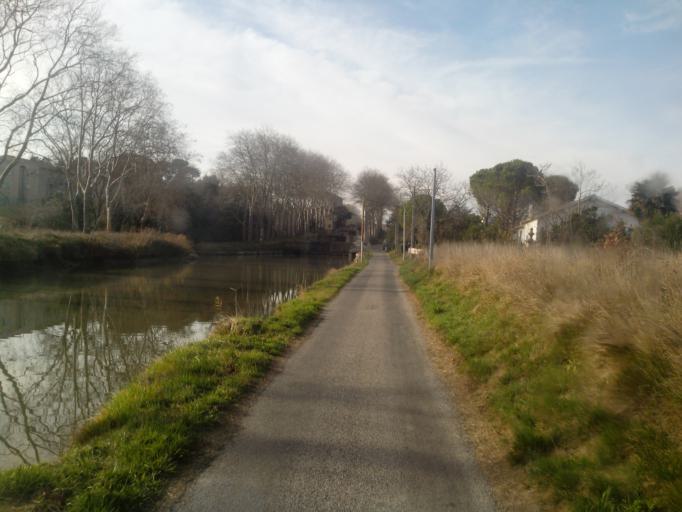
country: FR
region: Languedoc-Roussillon
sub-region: Departement de l'Aude
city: Castelnaudary
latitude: 43.3115
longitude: 1.9640
